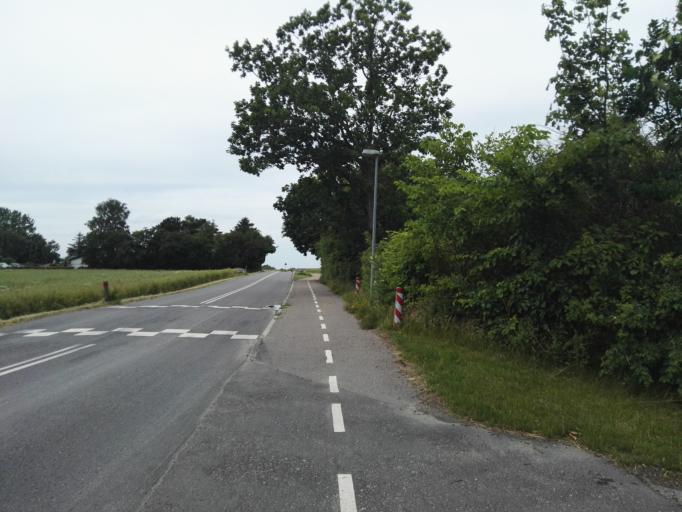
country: DK
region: Capital Region
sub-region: Hillerod Kommune
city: Skaevinge
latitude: 55.9075
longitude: 12.1774
